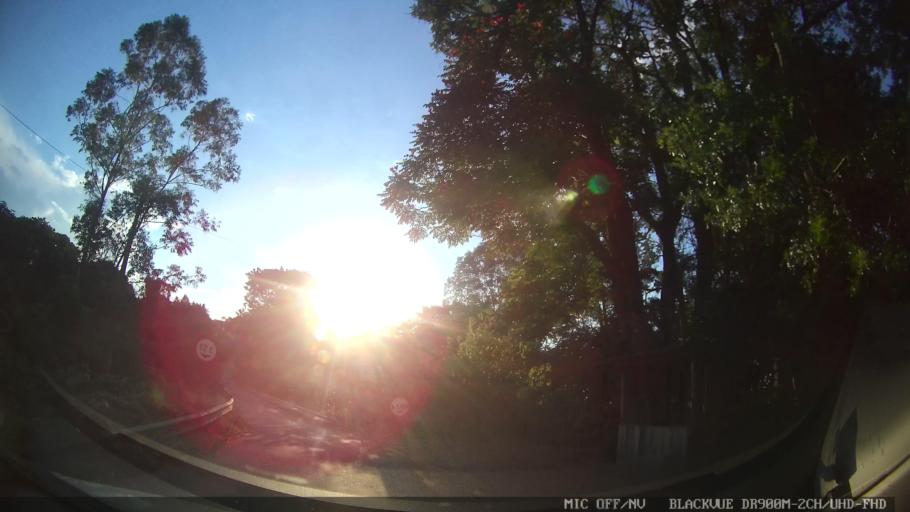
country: BR
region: Sao Paulo
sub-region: Braganca Paulista
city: Braganca Paulista
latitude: -22.9167
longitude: -46.4458
